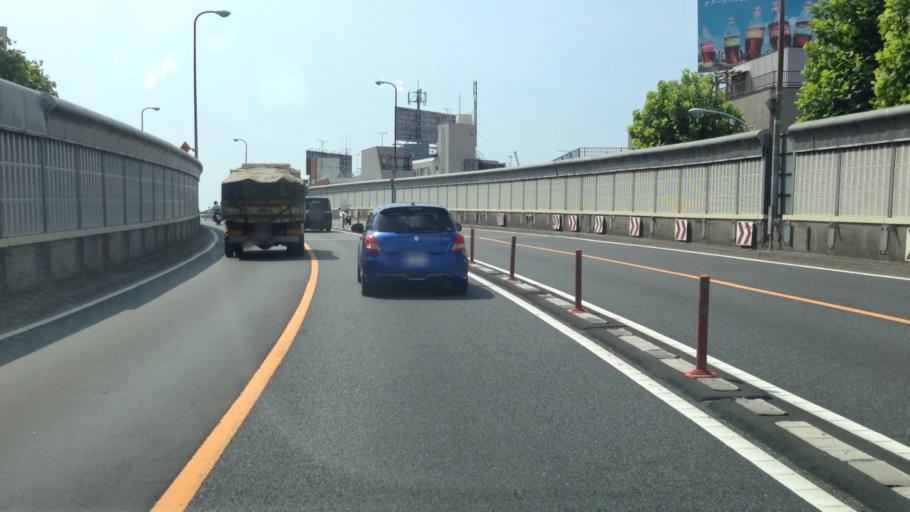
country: JP
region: Kanagawa
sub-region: Kawasaki-shi
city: Kawasaki
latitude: 35.5824
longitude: 139.7207
